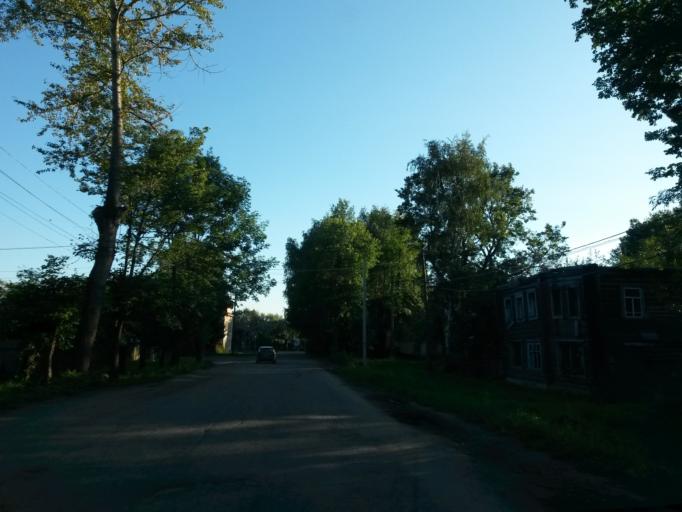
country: RU
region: Jaroslavl
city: Tutayev
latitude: 57.8822
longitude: 39.5442
